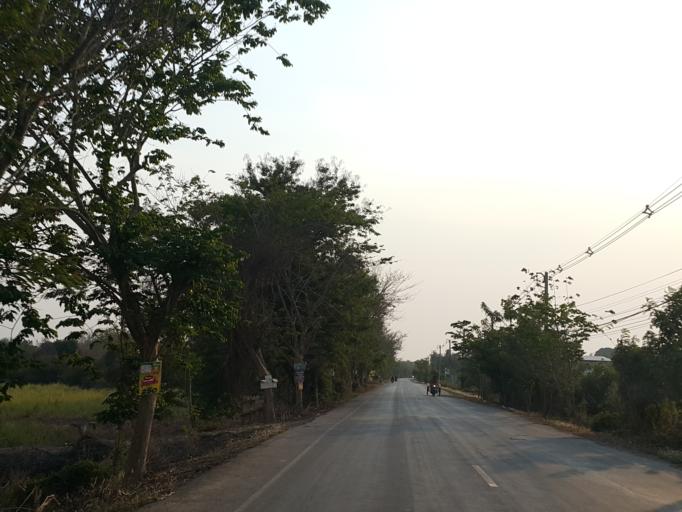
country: TH
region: Sukhothai
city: Si Samrong
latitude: 17.2143
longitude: 99.8784
